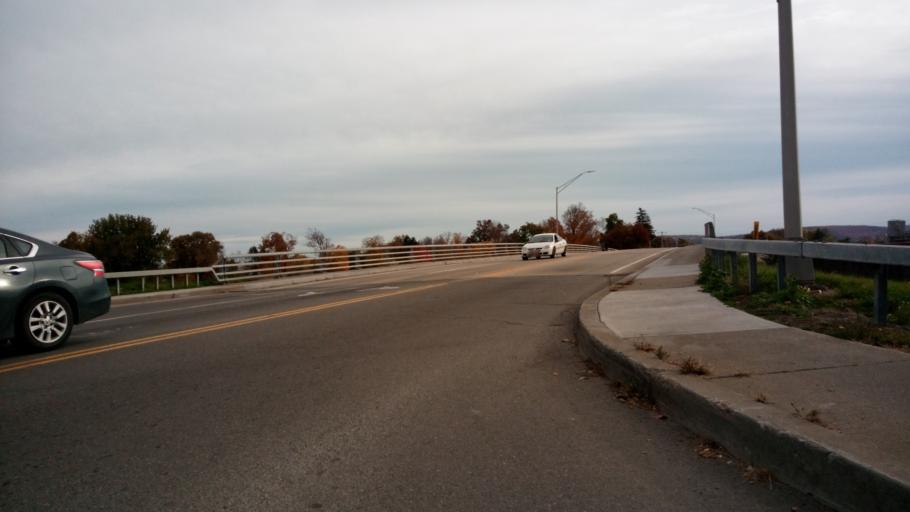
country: US
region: New York
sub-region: Chemung County
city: Elmira
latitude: 42.0885
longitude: -76.7980
